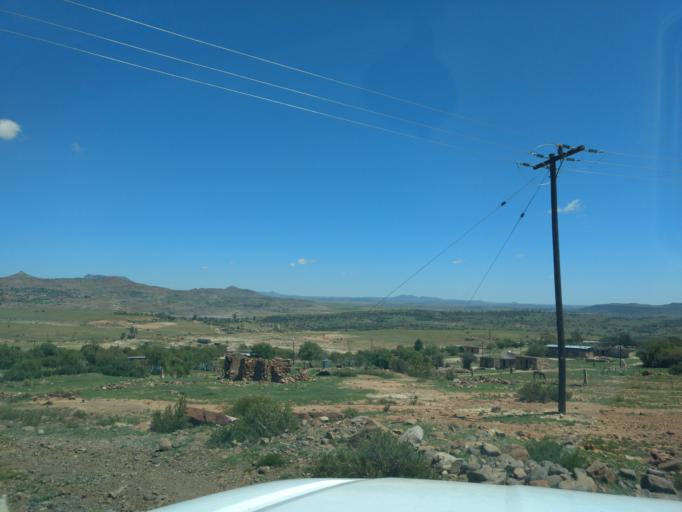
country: LS
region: Maseru
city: Maseru
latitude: -29.4564
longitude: 27.3754
